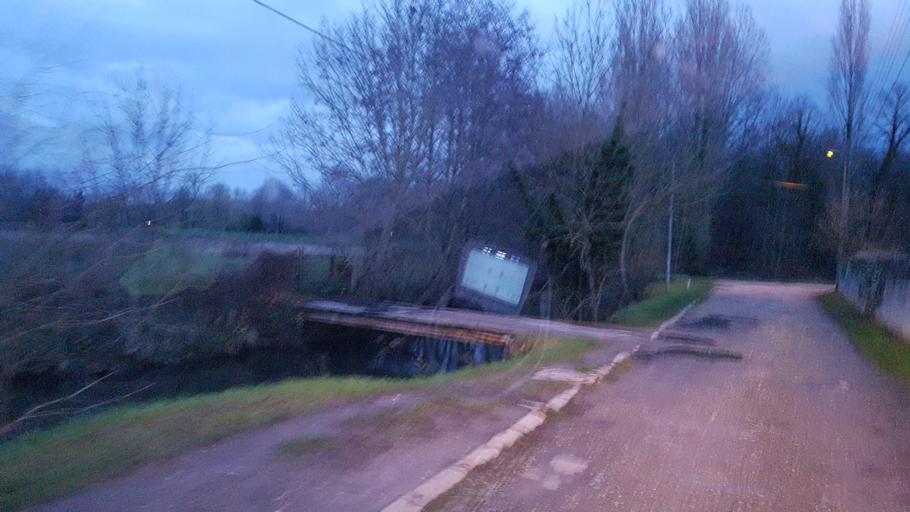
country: FR
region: Ile-de-France
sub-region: Departement de l'Essonne
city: Morigny-Champigny
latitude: 48.4411
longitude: 2.1712
